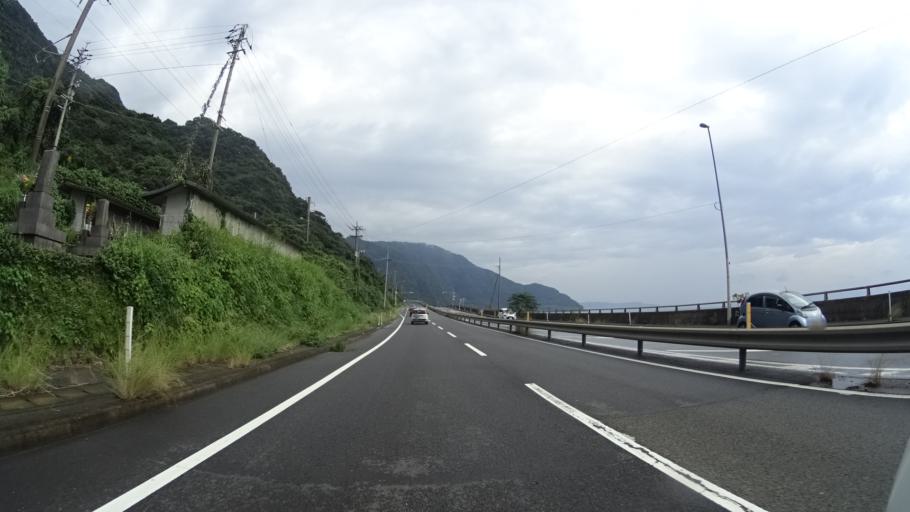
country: JP
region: Kagoshima
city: Kagoshima-shi
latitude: 31.6354
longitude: 130.6019
